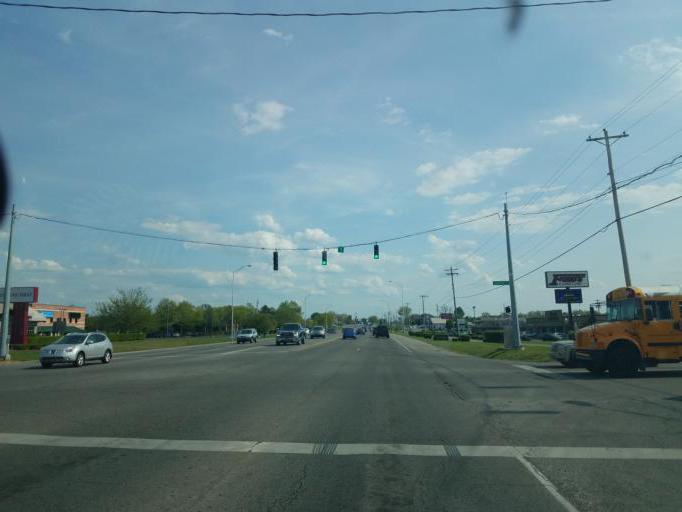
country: US
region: Kentucky
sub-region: Warren County
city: Bowling Green
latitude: 36.9699
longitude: -86.4341
